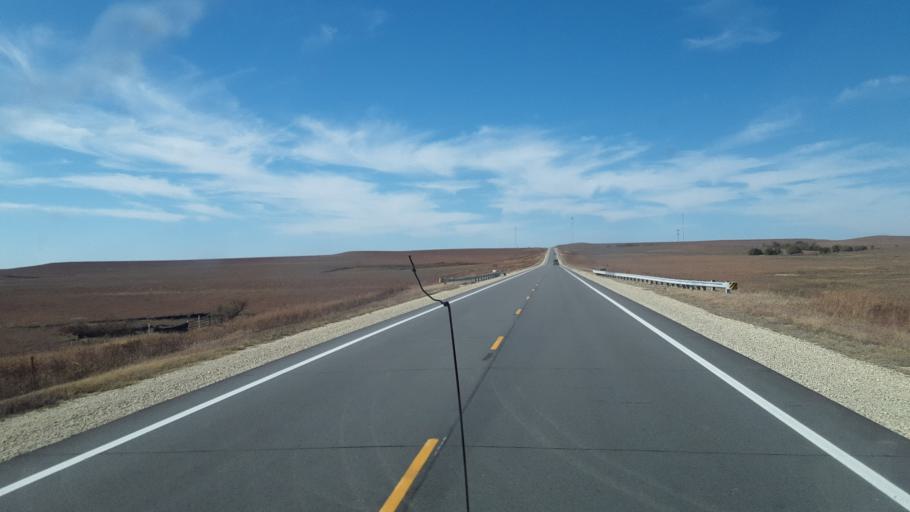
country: US
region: Kansas
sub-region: Chase County
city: Cottonwood Falls
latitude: 38.3627
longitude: -96.7094
